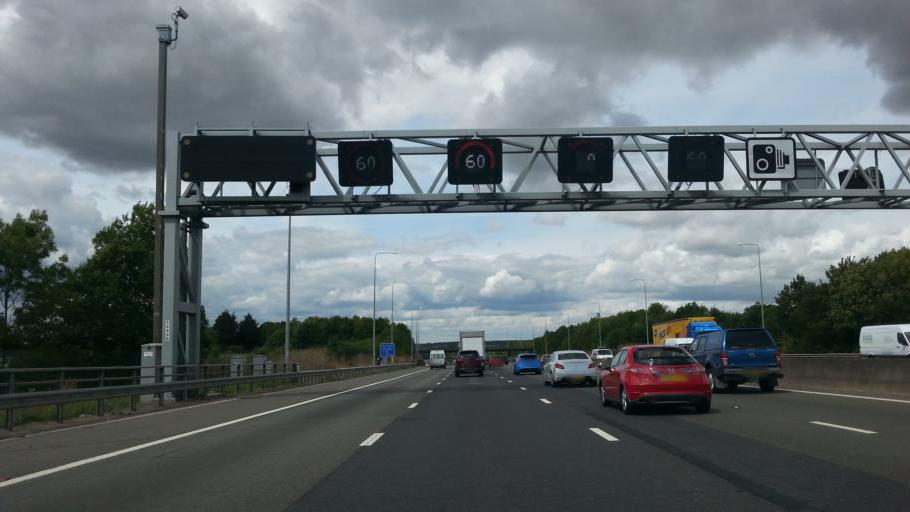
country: GB
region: England
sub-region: Greater London
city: Harold Wood
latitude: 51.6439
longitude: 0.2084
